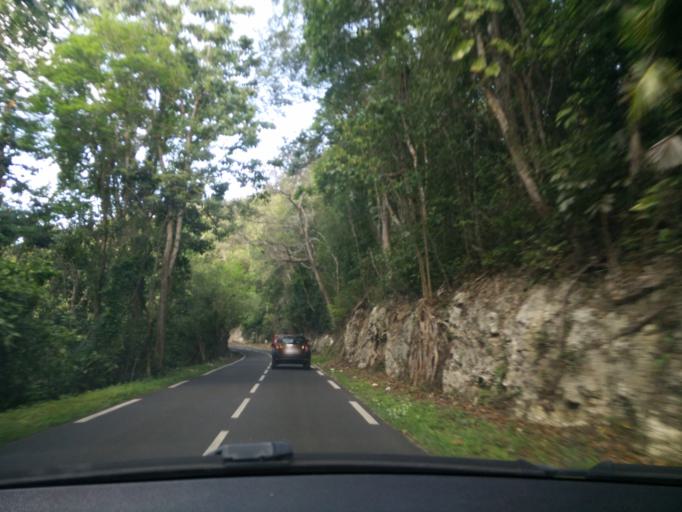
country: GP
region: Guadeloupe
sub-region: Guadeloupe
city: Sainte-Anne
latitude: 16.2653
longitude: -61.4219
